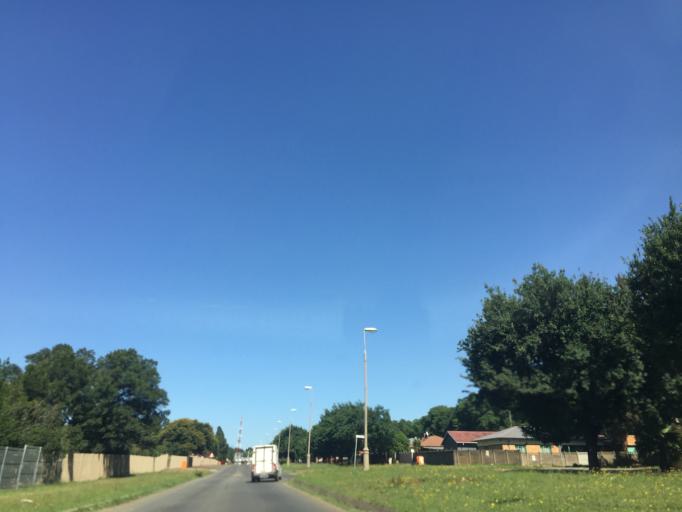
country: ZA
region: Gauteng
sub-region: Sedibeng District Municipality
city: Vanderbijlpark
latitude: -26.7046
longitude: 27.8449
